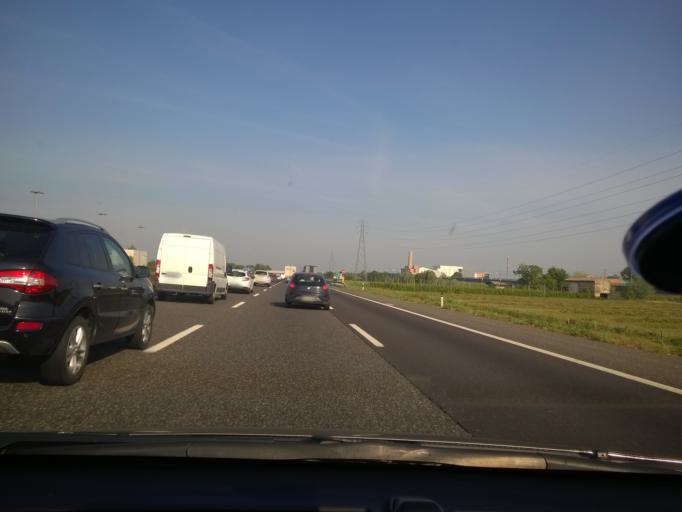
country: IT
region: Emilia-Romagna
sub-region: Provincia di Parma
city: Parma
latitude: 44.8319
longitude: 10.3653
